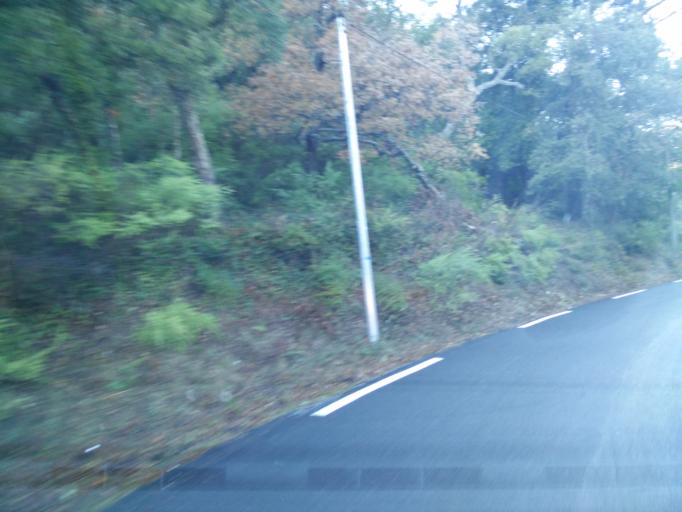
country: FR
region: Provence-Alpes-Cote d'Azur
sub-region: Departement du Var
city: Collobrieres
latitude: 43.2368
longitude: 6.3342
